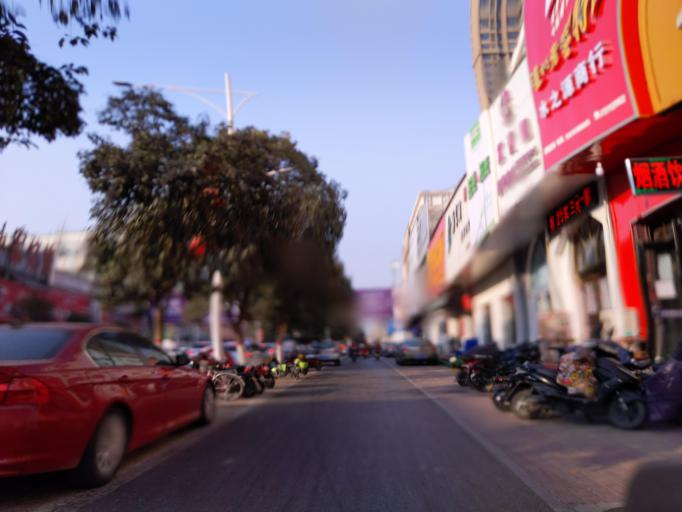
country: CN
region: Henan Sheng
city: Puyang
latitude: 35.7759
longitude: 115.0330
